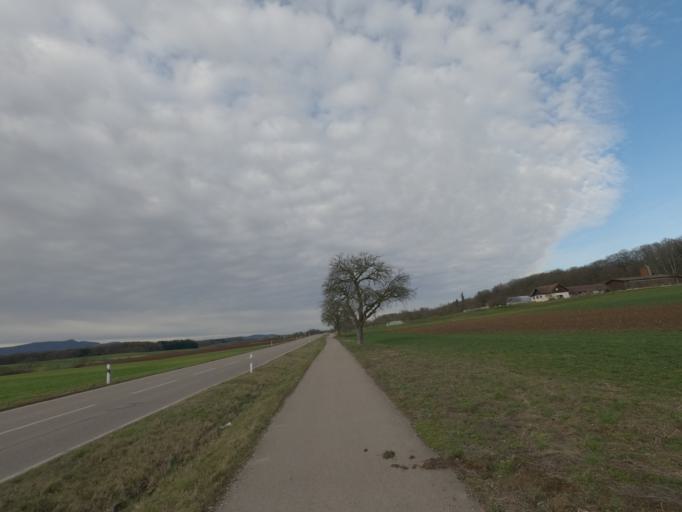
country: DE
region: Baden-Wuerttemberg
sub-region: Regierungsbezirk Stuttgart
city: Zell unter Aichelberg
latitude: 48.6530
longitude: 9.5642
